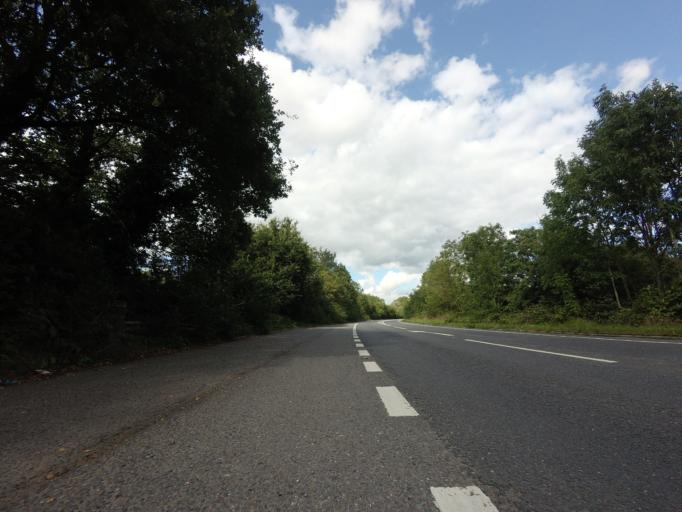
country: GB
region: England
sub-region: Kent
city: Borough Green
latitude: 51.2900
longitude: 0.2841
